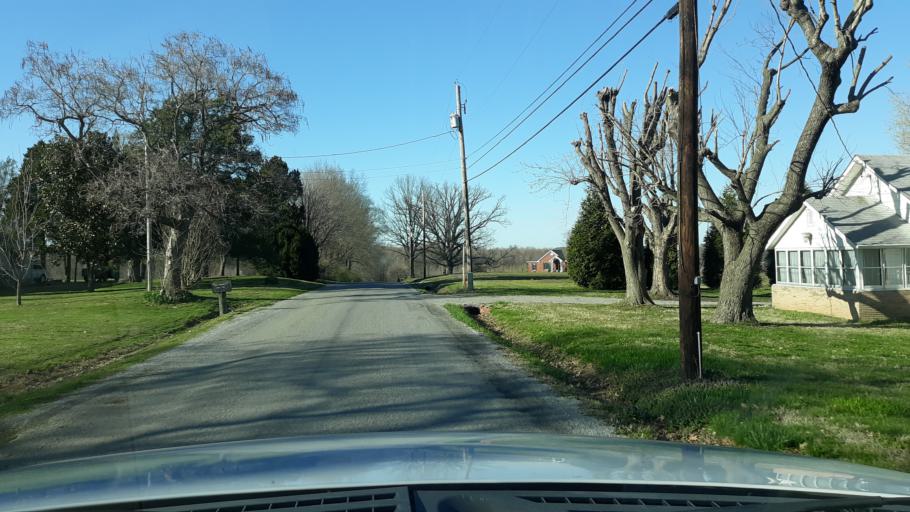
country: US
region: Illinois
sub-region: Saline County
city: Harrisburg
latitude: 37.7532
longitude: -88.5680
